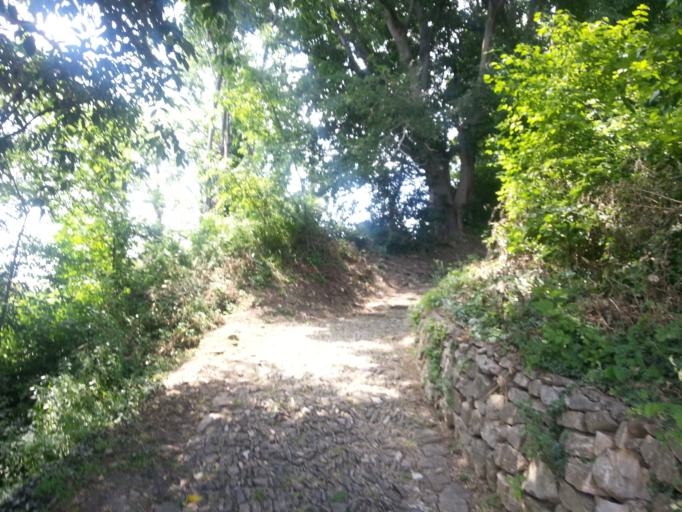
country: IT
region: Lombardy
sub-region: Provincia di Lecco
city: Montevecchia
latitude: 45.7013
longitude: 9.3785
